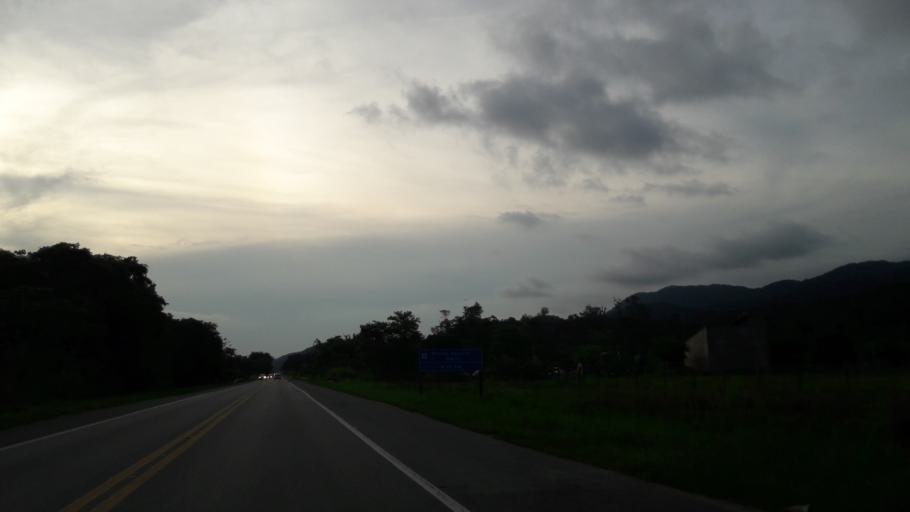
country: BR
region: Sao Paulo
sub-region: Peruibe
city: Peruibe
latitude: -24.2976
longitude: -47.0716
